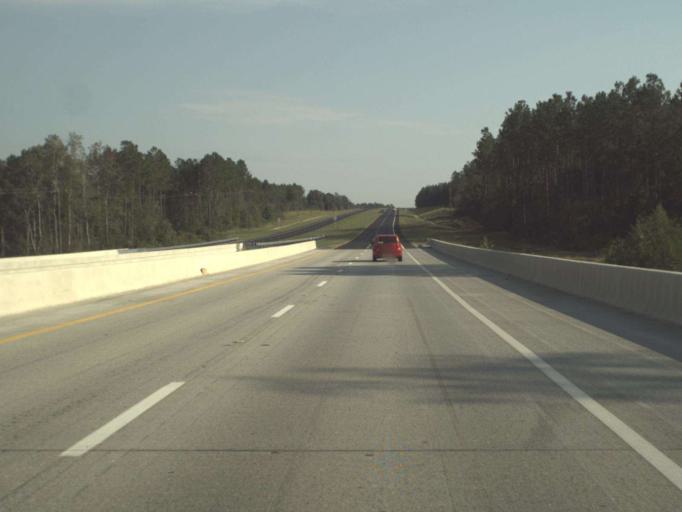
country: US
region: Florida
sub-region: Walton County
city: Freeport
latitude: 30.5283
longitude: -85.8382
